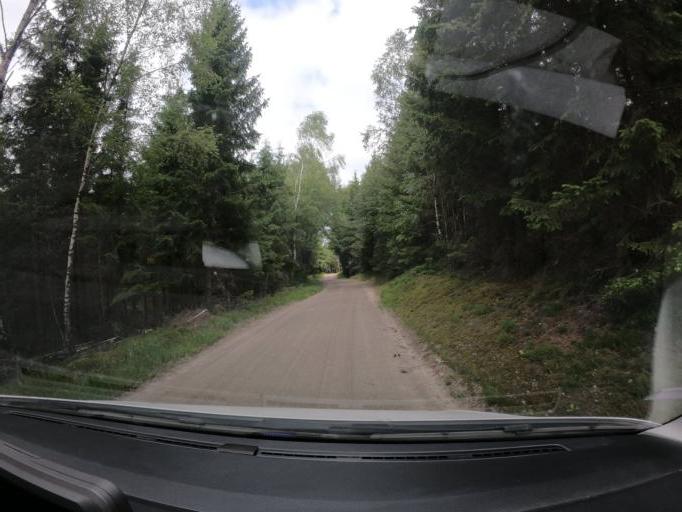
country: SE
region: Skane
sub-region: Hassleholms Kommun
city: Sosdala
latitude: 56.0603
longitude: 13.5805
